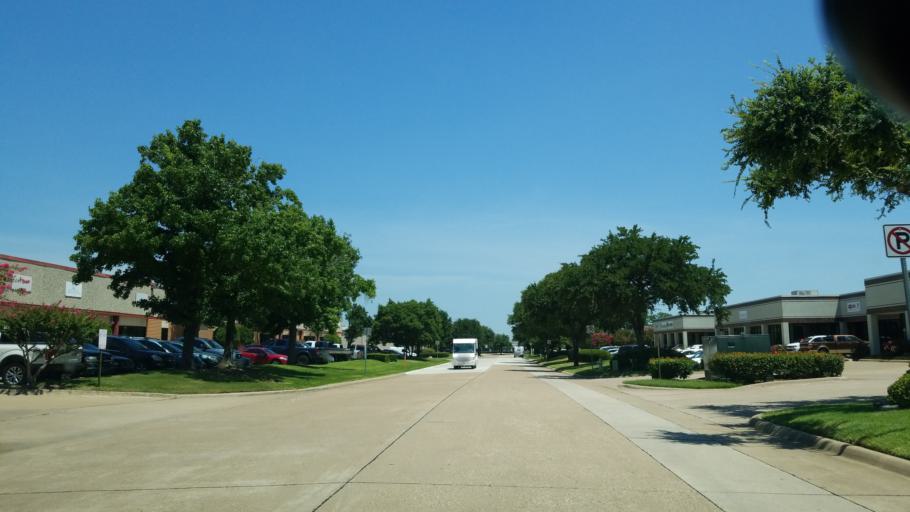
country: US
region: Texas
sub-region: Dallas County
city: Farmers Branch
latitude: 32.9200
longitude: -96.9271
